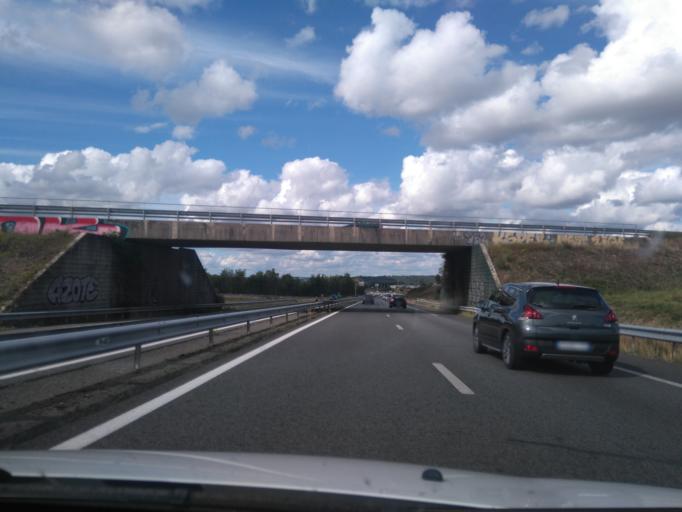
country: FR
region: Brittany
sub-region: Departement d'Ille-et-Vilaine
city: Bain-de-Bretagne
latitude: 47.8502
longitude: -1.6950
